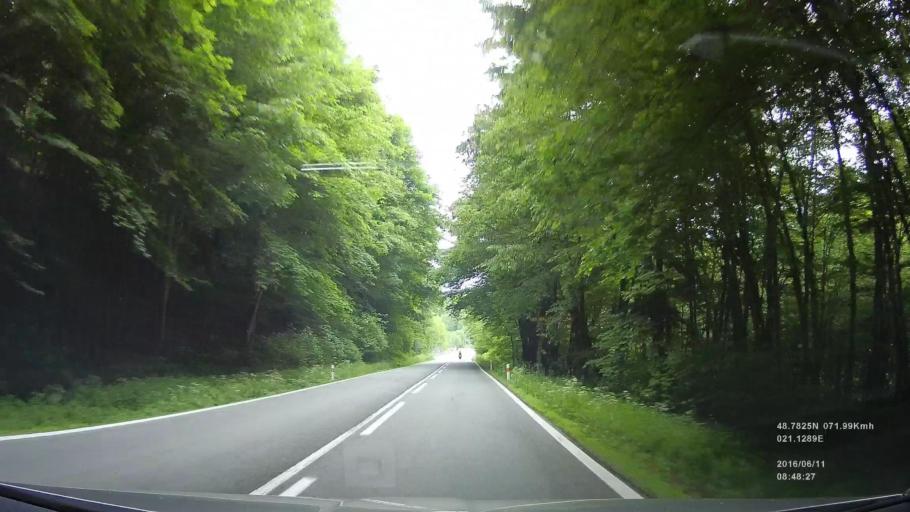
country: SK
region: Kosicky
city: Kosice
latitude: 48.7690
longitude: 21.1660
